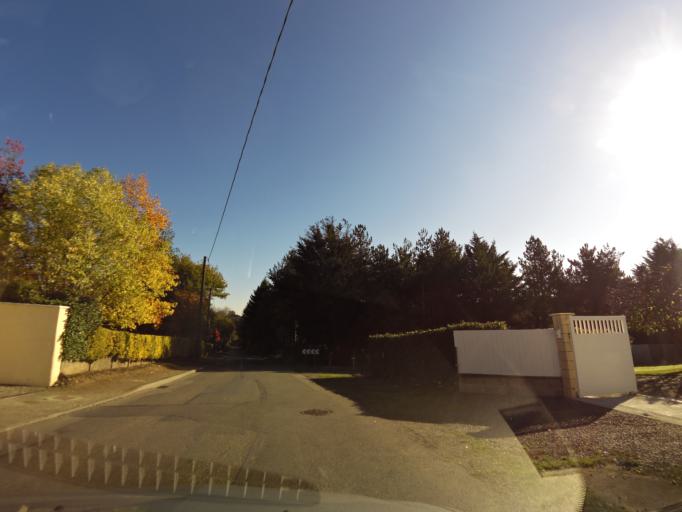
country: FR
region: Brittany
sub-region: Departement d'Ille-et-Vilaine
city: Pance
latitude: 47.8752
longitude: -1.6855
